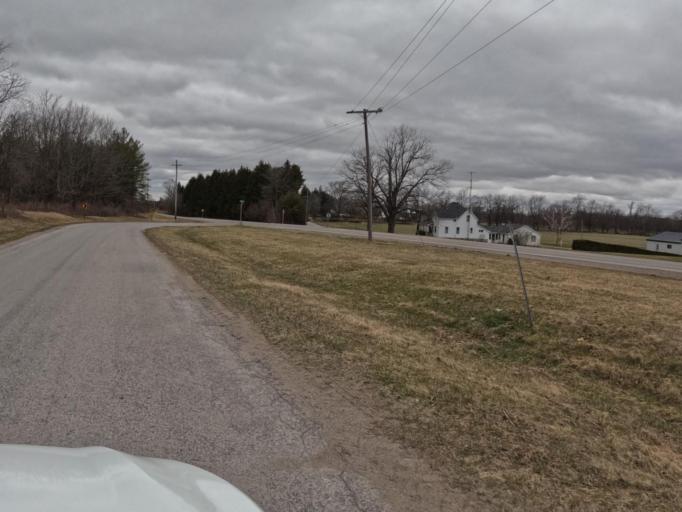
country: CA
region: Ontario
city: Norfolk County
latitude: 42.9400
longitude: -80.4232
